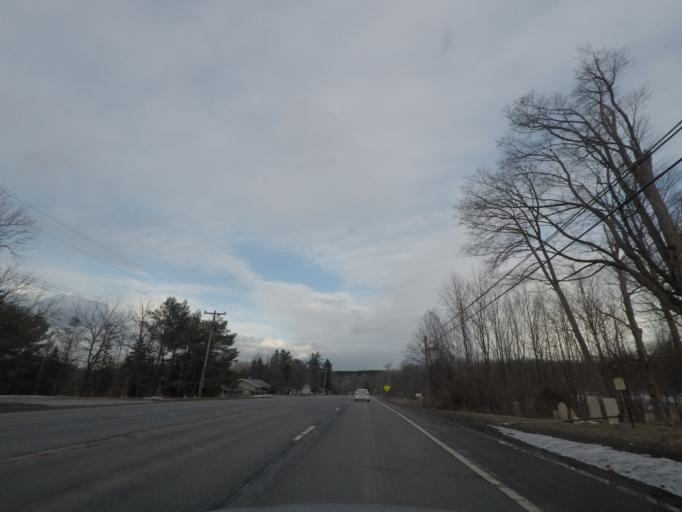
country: US
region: New York
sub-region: Oneida County
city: Clark Mills
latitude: 43.0759
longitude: -75.4431
